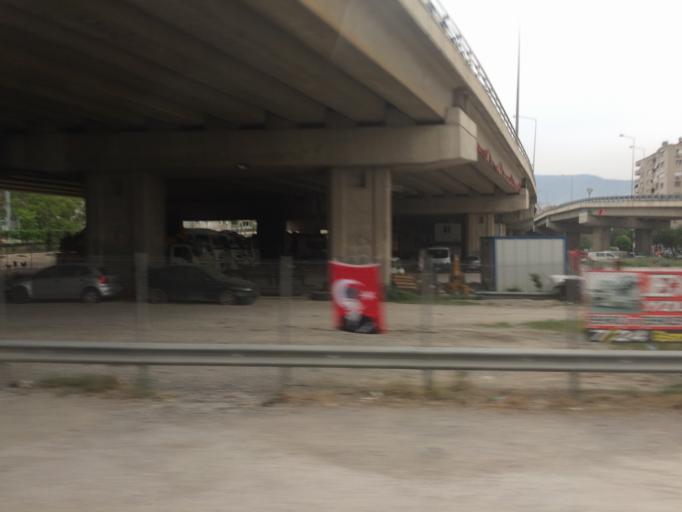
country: TR
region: Izmir
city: Bornova
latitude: 38.4581
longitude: 27.2069
